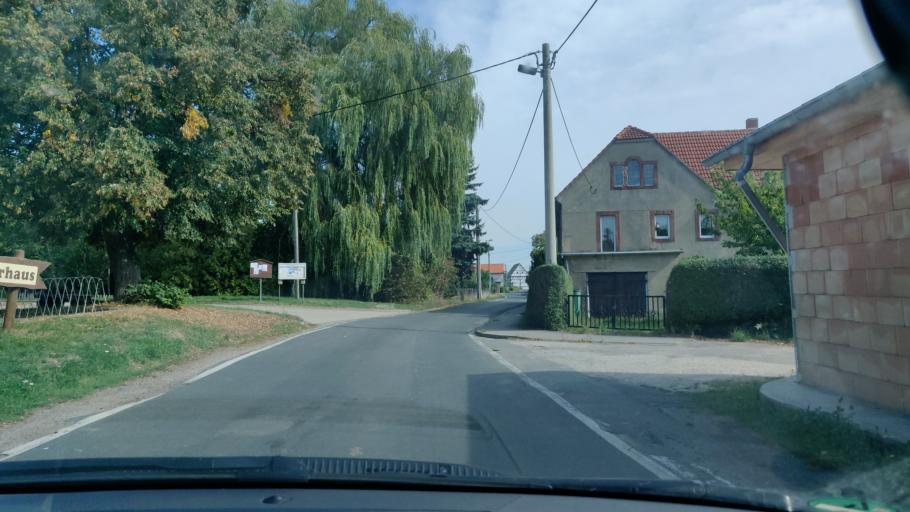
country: DE
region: Saxony
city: Konigsfeld
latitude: 51.0875
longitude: 12.7723
